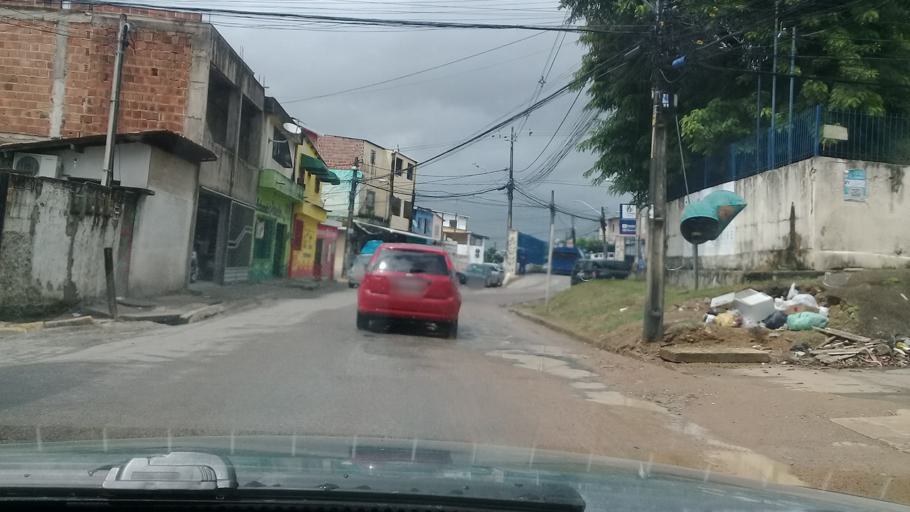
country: BR
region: Pernambuco
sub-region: Jaboatao Dos Guararapes
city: Jaboatao dos Guararapes
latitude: -8.1146
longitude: -34.9535
